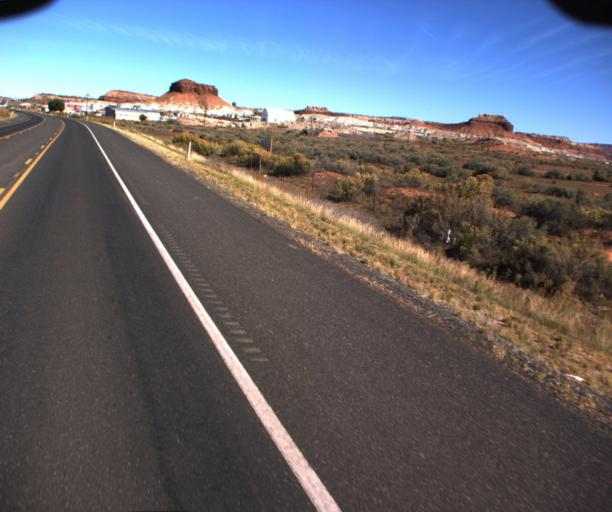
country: US
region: Arizona
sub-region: Coconino County
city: Fredonia
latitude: 36.9660
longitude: -112.5269
